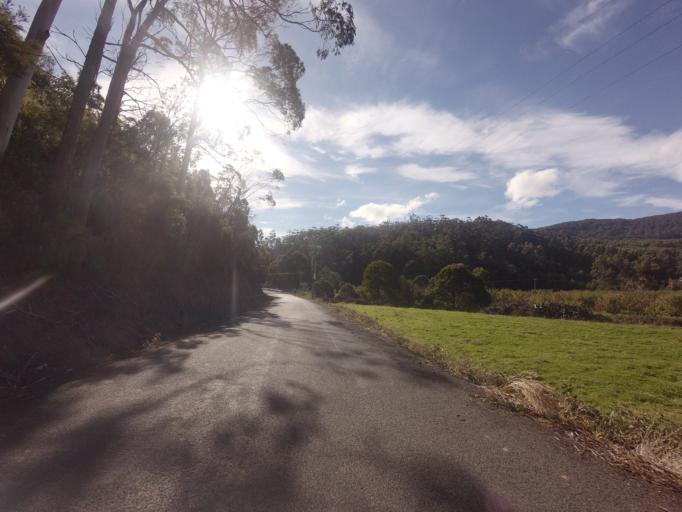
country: AU
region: Tasmania
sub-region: Clarence
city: Sandford
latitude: -43.1198
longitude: 147.7587
